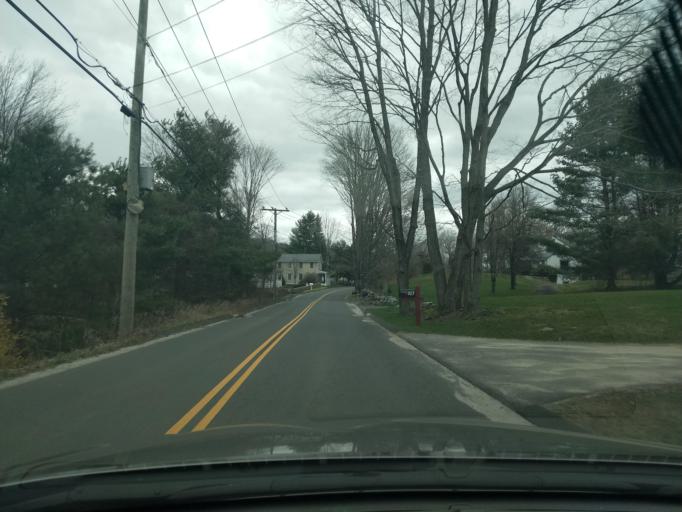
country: US
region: Connecticut
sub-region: Fairfield County
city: Newtown
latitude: 41.3574
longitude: -73.2857
